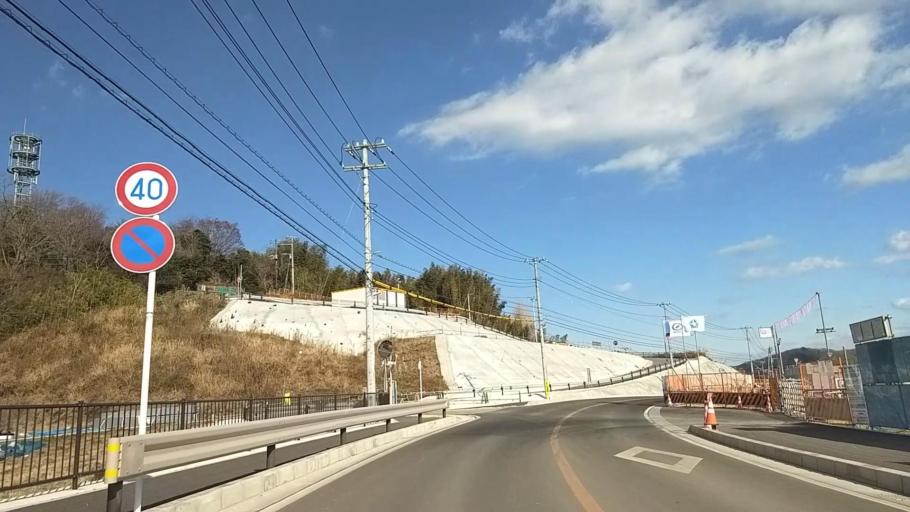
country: JP
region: Kanagawa
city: Isehara
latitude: 35.4172
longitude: 139.2858
